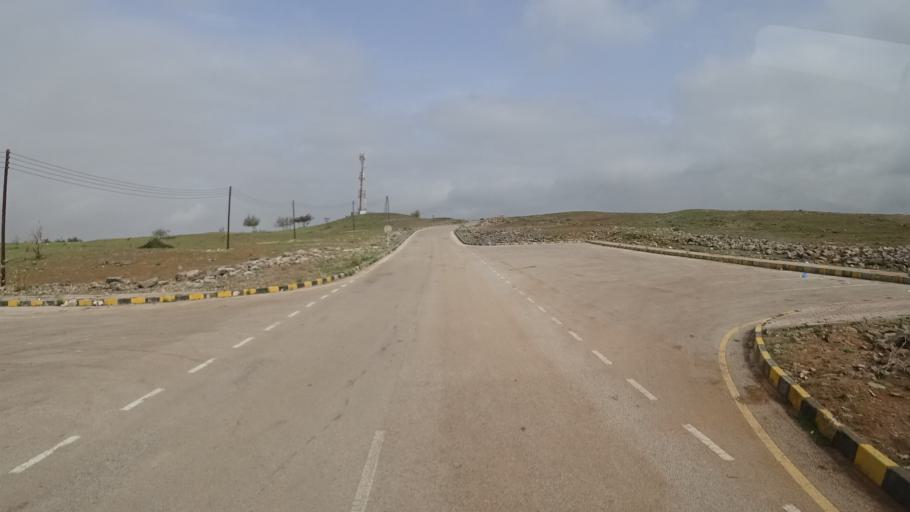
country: OM
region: Zufar
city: Salalah
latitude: 17.0780
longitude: 54.4476
